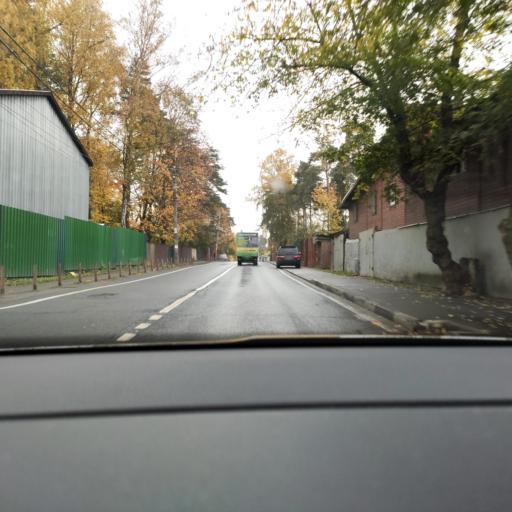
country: RU
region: Moskovskaya
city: Druzhba
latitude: 55.8866
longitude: 37.7391
